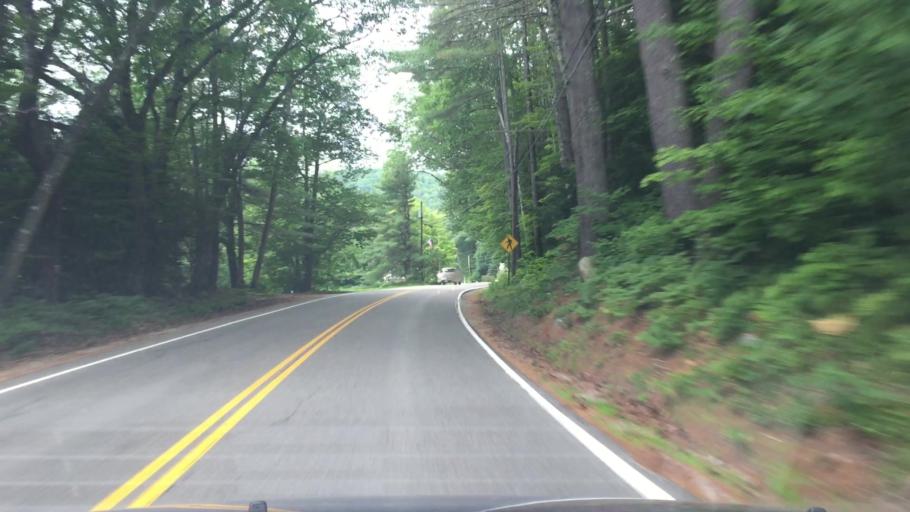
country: US
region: New Hampshire
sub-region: Carroll County
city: Madison
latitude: 43.9125
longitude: -71.0781
